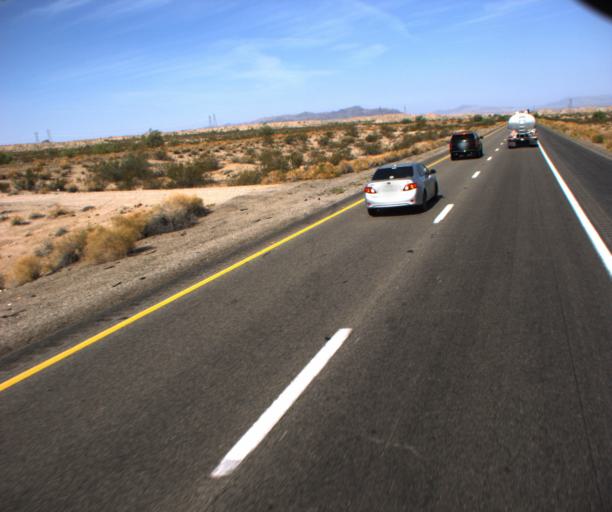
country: US
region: Arizona
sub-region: Mohave County
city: Desert Hills
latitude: 34.7280
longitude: -114.3712
